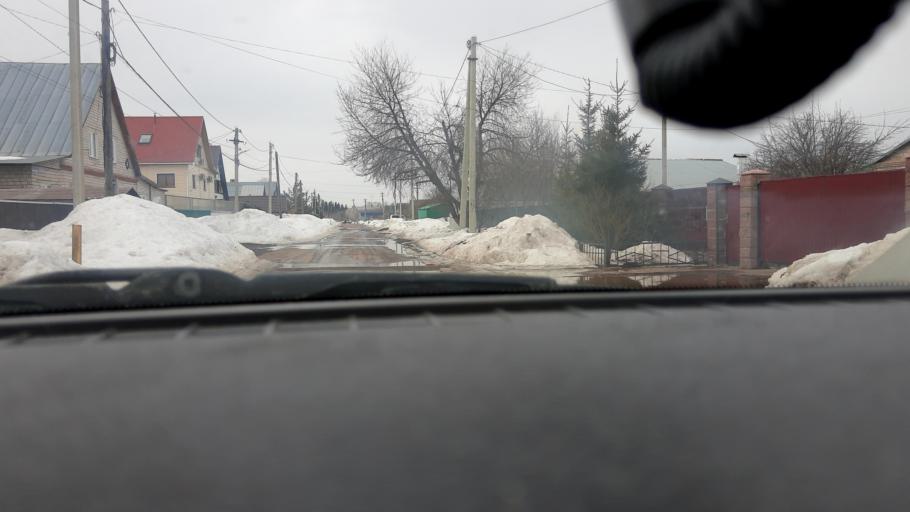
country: RU
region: Bashkortostan
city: Avdon
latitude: 54.6107
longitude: 55.8545
